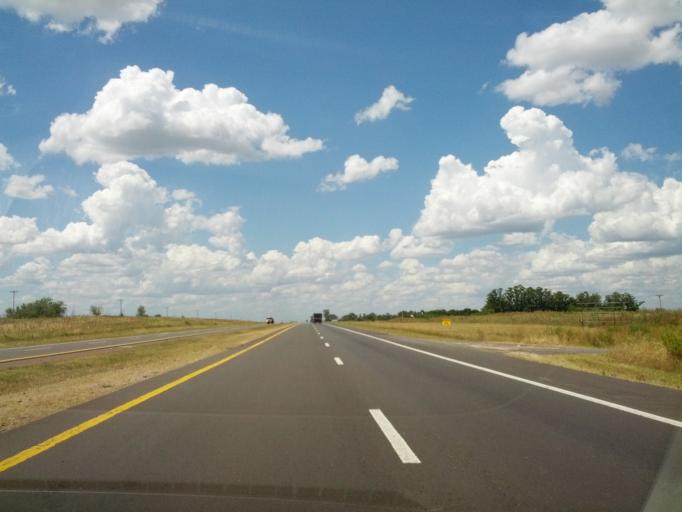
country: AR
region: Entre Rios
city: Concepcion del Uruguay
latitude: -32.5305
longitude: -58.3352
